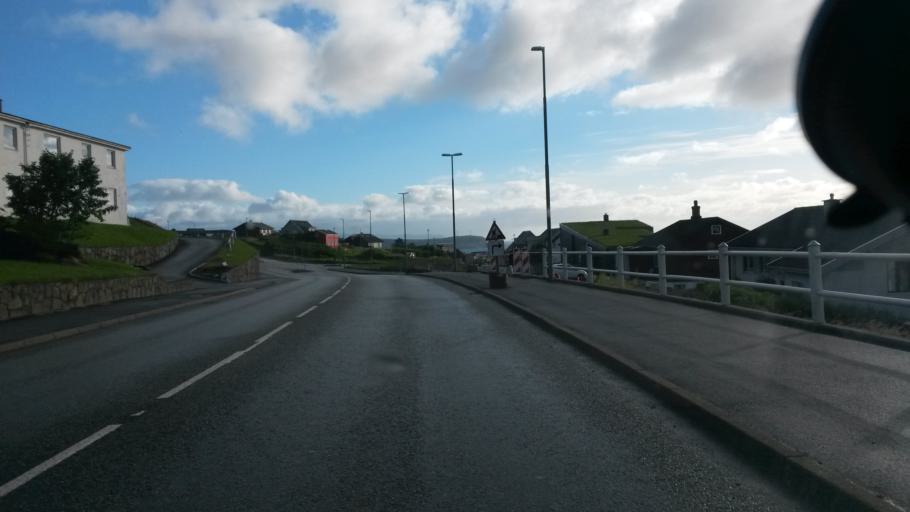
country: FO
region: Streymoy
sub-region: Torshavn
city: Torshavn
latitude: 62.0130
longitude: -6.7898
